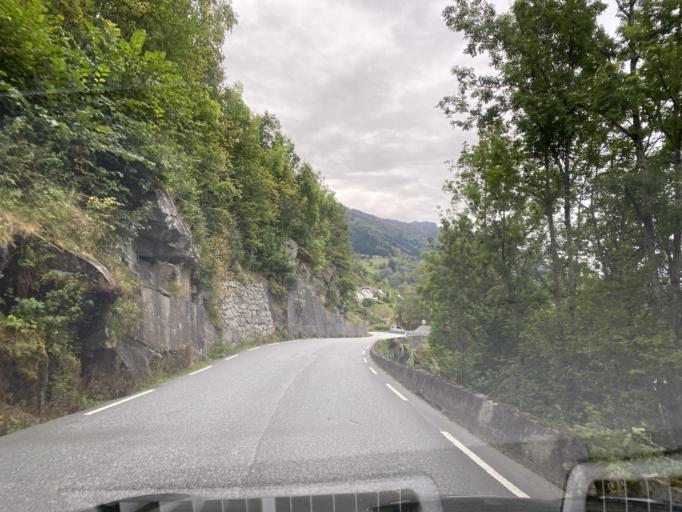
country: NO
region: Hordaland
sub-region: Odda
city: Odda
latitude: 60.2151
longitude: 6.6027
